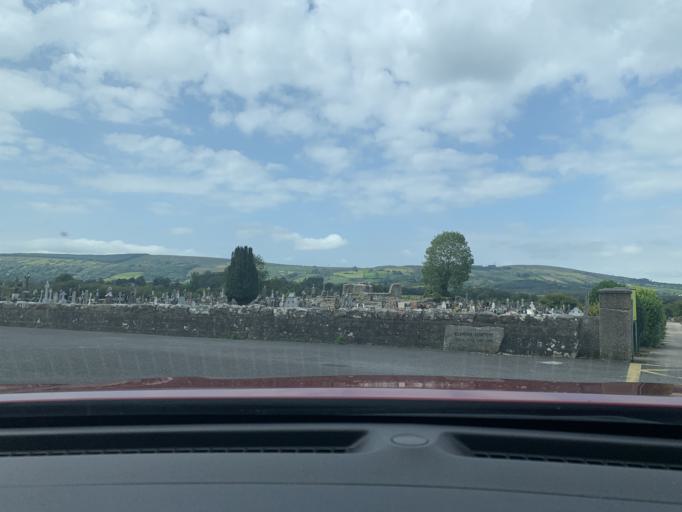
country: IE
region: Connaught
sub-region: Maigh Eo
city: Kiltamagh
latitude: 53.8407
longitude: -9.0158
